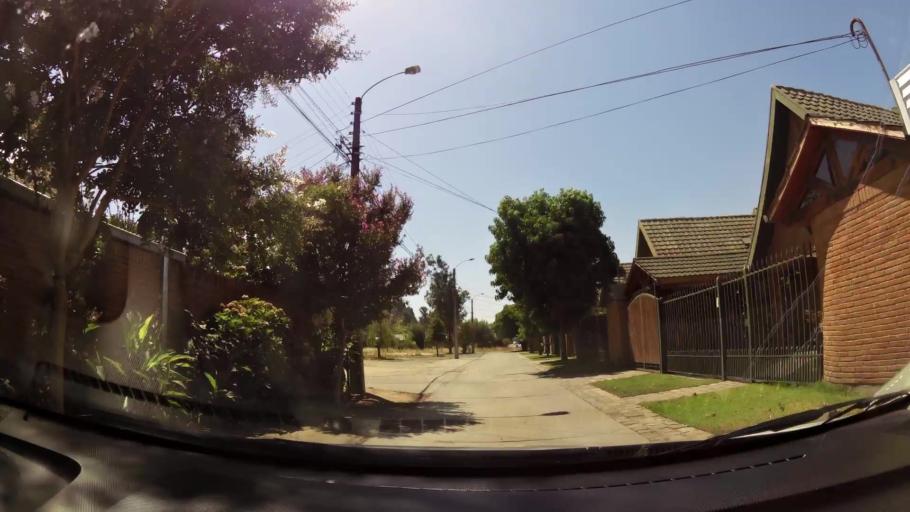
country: CL
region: Maule
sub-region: Provincia de Talca
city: Talca
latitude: -35.4240
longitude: -71.6262
